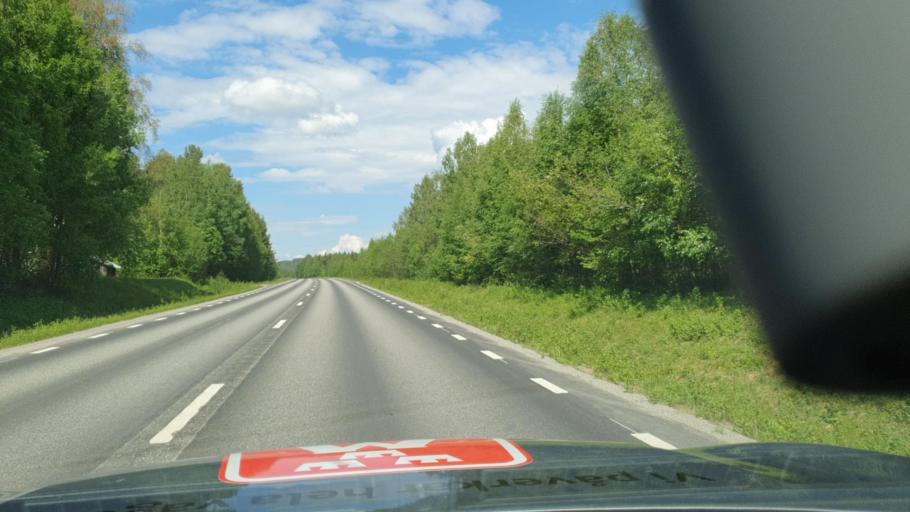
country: SE
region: Vaesternorrland
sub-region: Solleftea Kommun
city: As
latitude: 63.6183
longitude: 16.8203
